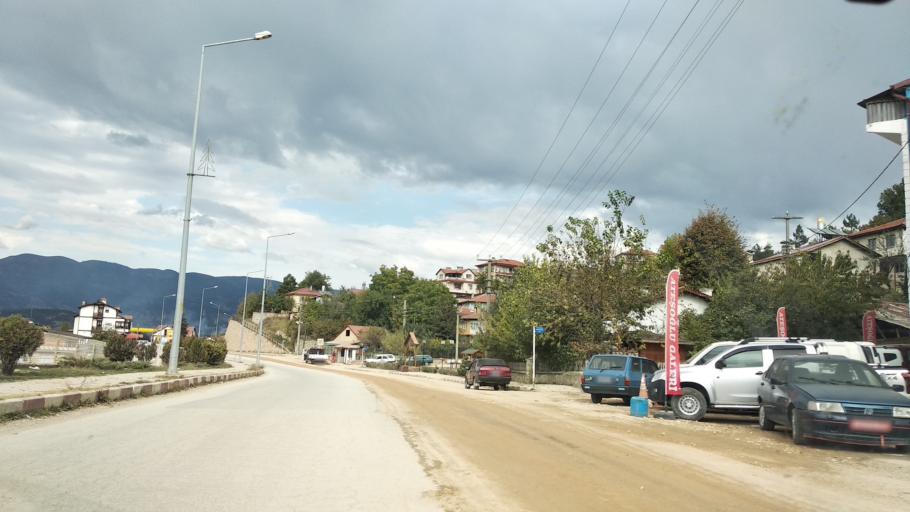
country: TR
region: Bolu
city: Mudurnu
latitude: 40.4716
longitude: 31.2099
